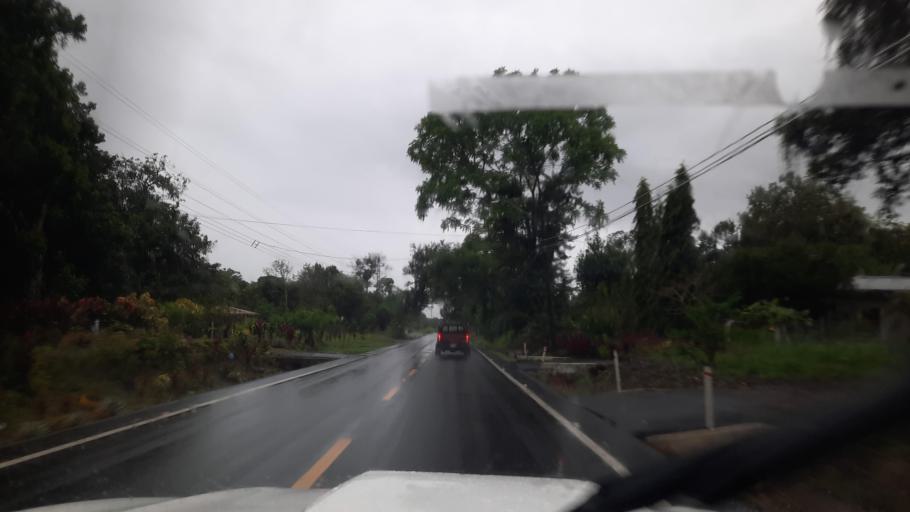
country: PA
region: Chiriqui
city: Sortova
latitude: 8.5575
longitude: -82.6274
